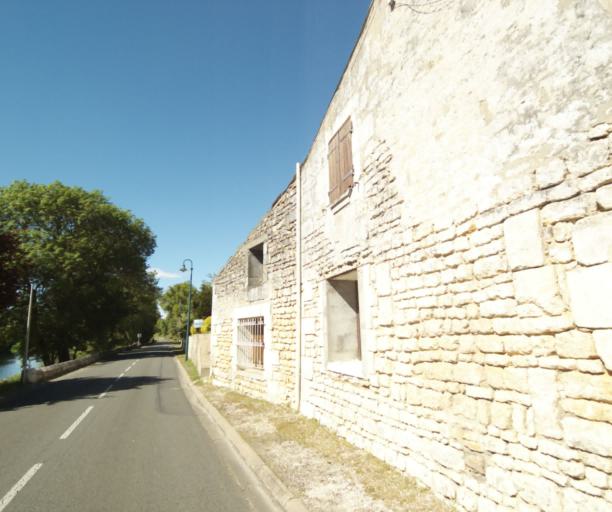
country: FR
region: Poitou-Charentes
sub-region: Departement de la Charente-Maritime
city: Bussac-sur-Charente
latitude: 45.8207
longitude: -0.6386
